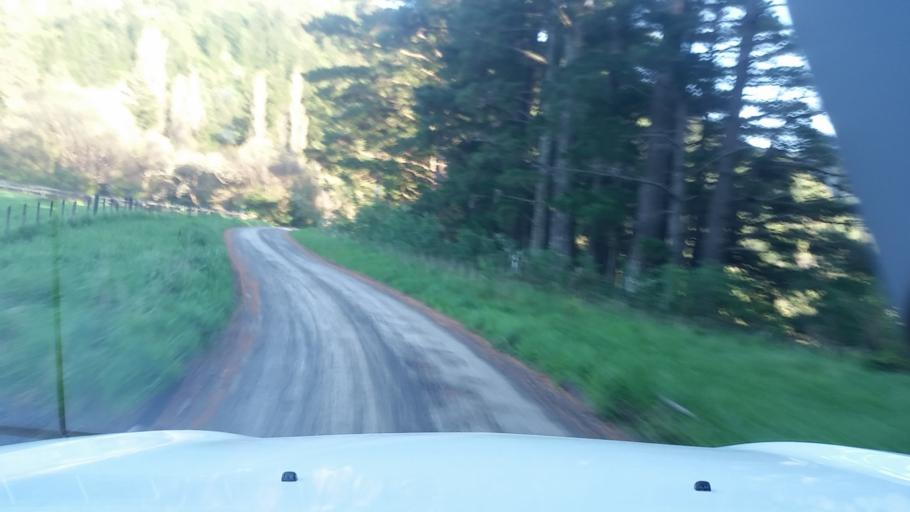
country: NZ
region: Wellington
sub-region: Masterton District
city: Masterton
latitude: -41.0442
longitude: 175.3944
